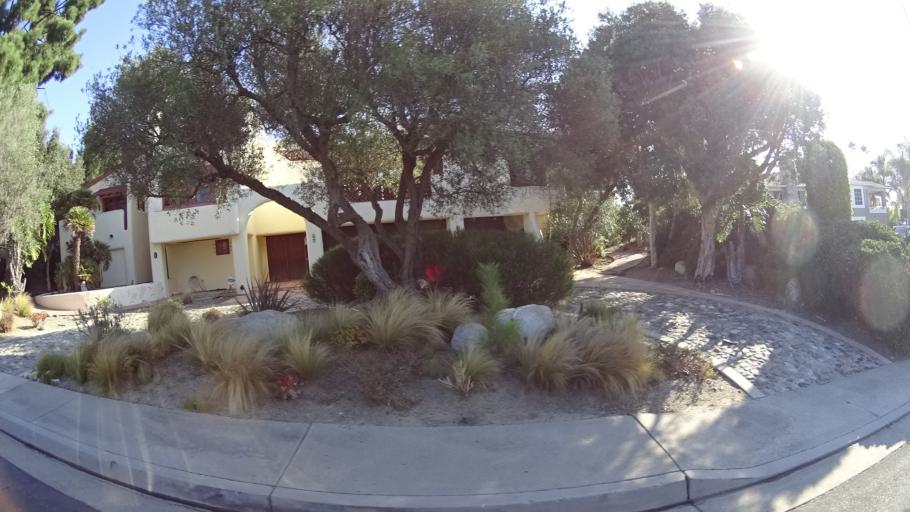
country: US
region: California
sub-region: Orange County
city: San Clemente
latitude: 33.4185
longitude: -117.5890
